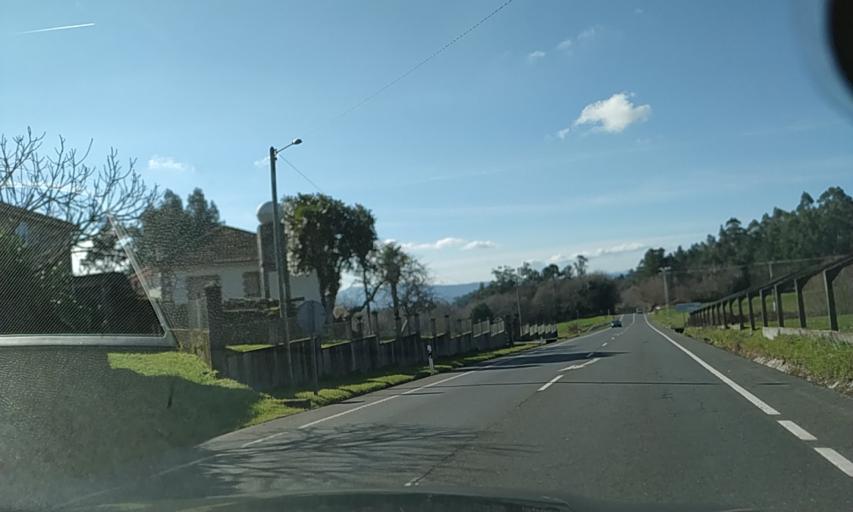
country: ES
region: Galicia
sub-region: Provincia da Coruna
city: Ribeira
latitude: 42.7068
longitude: -8.4134
